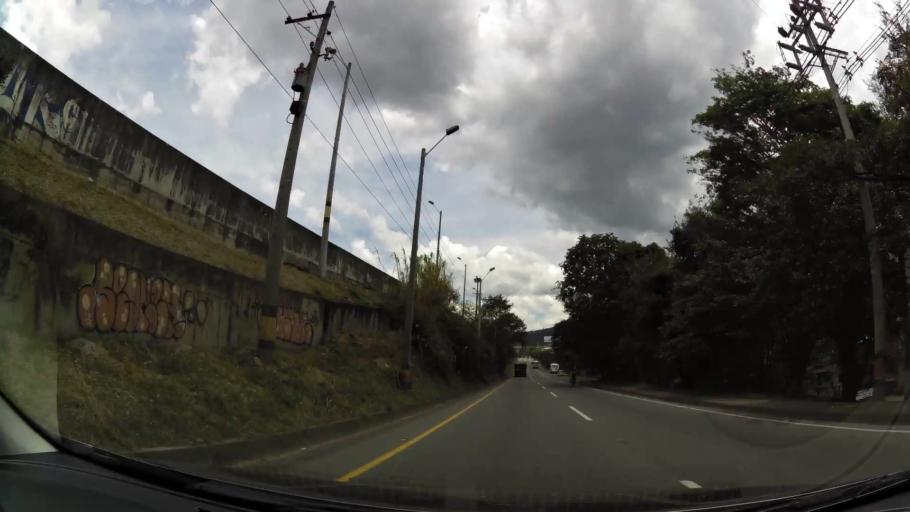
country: CO
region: Antioquia
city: Municipio de Copacabana
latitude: 6.3495
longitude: -75.5163
